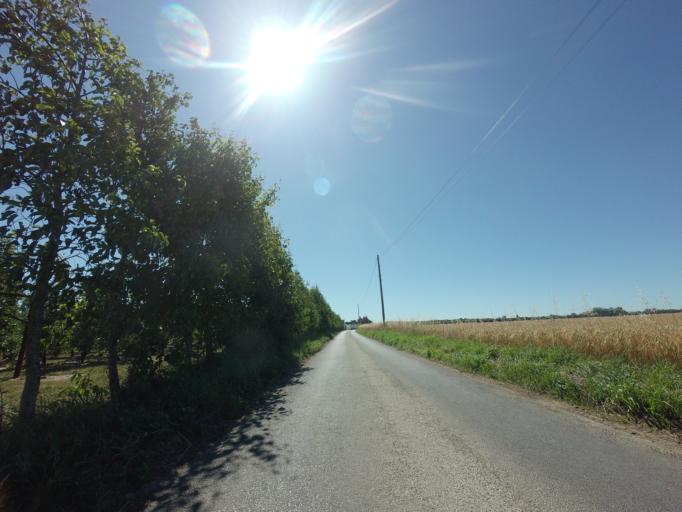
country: GB
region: England
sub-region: Kent
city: Ash
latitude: 51.2940
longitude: 1.2441
